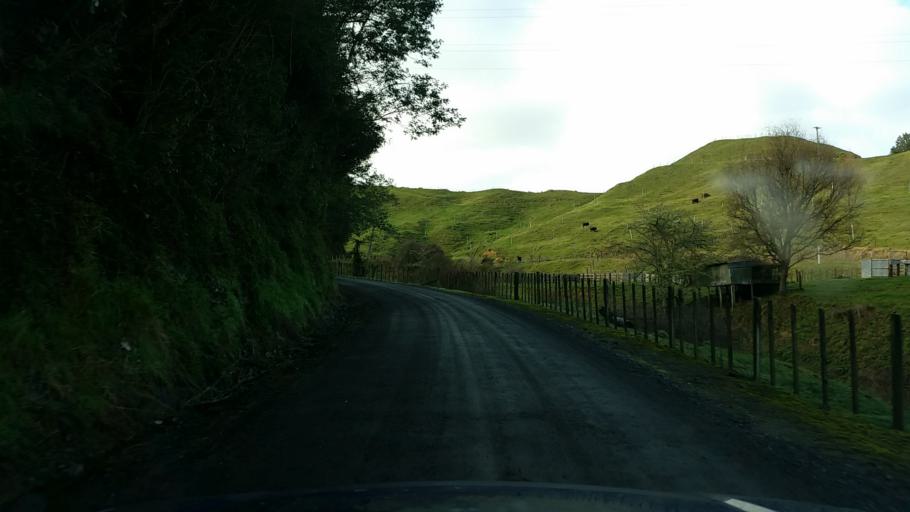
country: NZ
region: Taranaki
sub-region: New Plymouth District
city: Waitara
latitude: -39.0726
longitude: 174.7954
